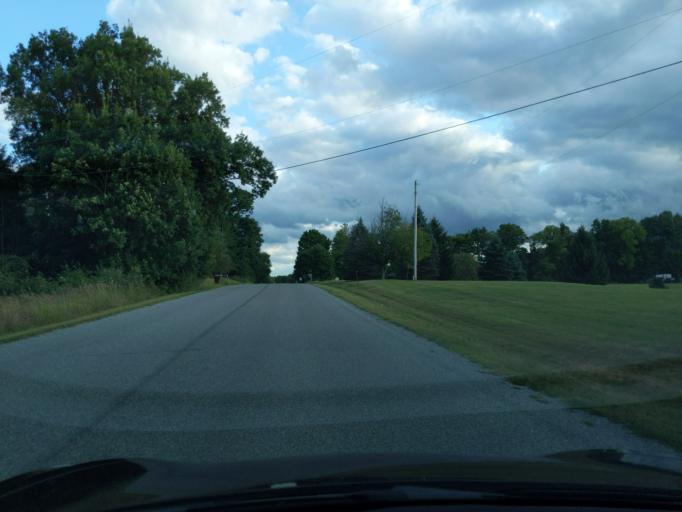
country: US
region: Michigan
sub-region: Ingham County
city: Holt
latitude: 42.6022
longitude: -84.5823
